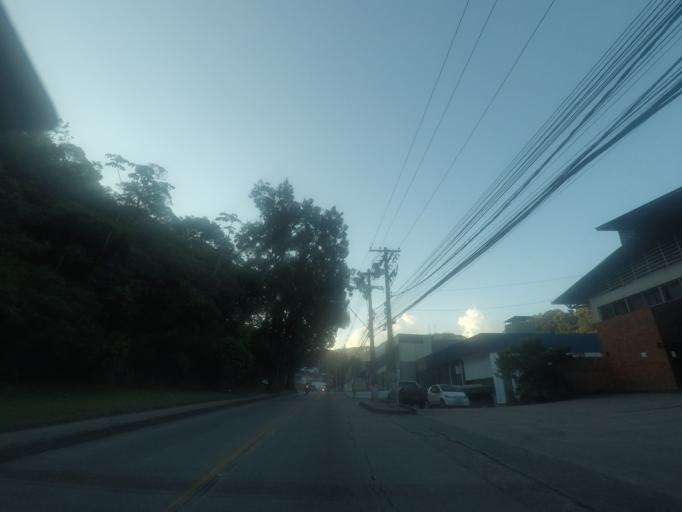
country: BR
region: Rio de Janeiro
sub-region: Petropolis
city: Petropolis
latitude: -22.5333
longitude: -43.2094
